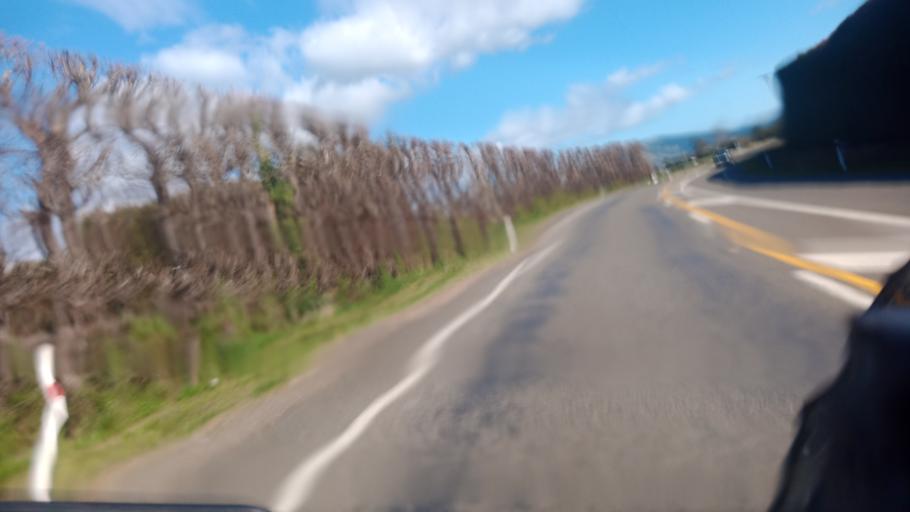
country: NZ
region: Bay of Plenty
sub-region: Opotiki District
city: Opotiki
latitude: -38.0009
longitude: 177.2975
